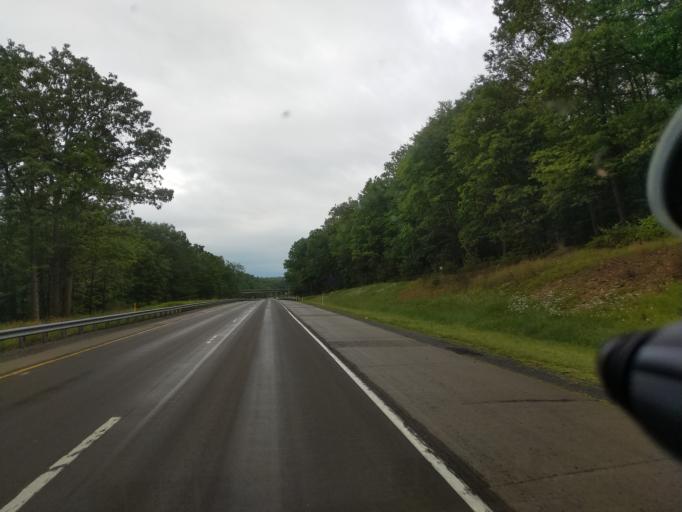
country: US
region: Pennsylvania
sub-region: Union County
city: Mifflinburg
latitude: 41.0430
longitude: -77.1288
